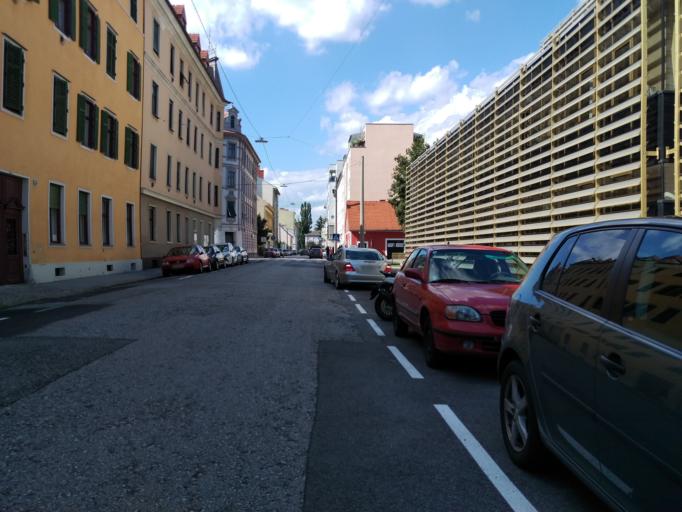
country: AT
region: Styria
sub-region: Graz Stadt
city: Graz
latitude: 47.0601
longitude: 15.4332
